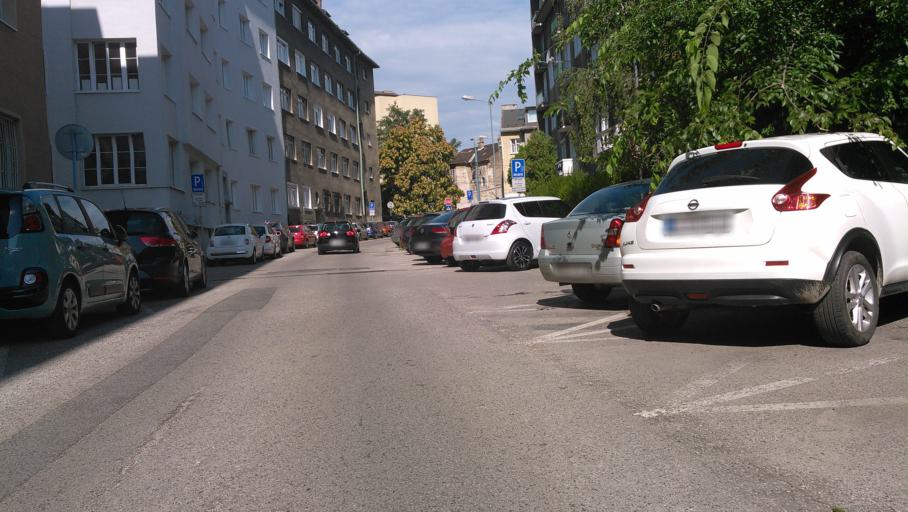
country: SK
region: Bratislavsky
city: Bratislava
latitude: 48.1558
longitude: 17.1141
